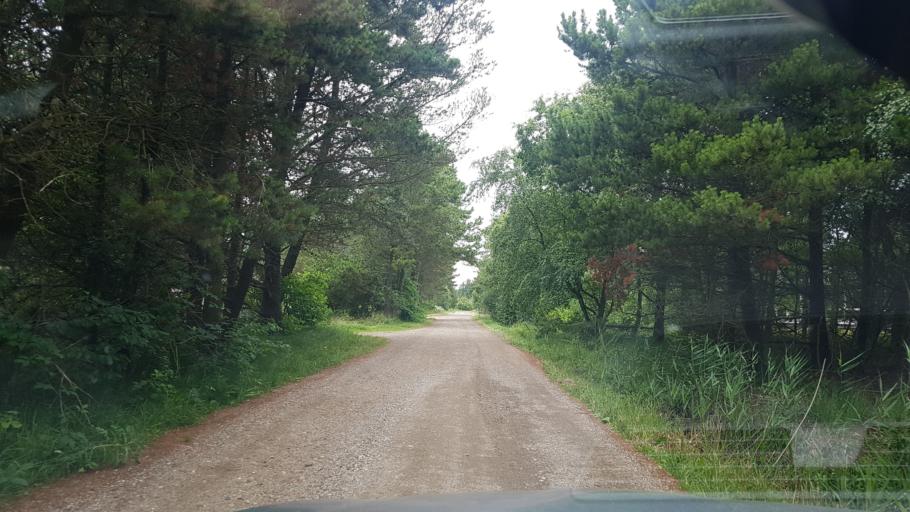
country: DE
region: Schleswig-Holstein
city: List
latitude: 55.0902
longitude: 8.5288
